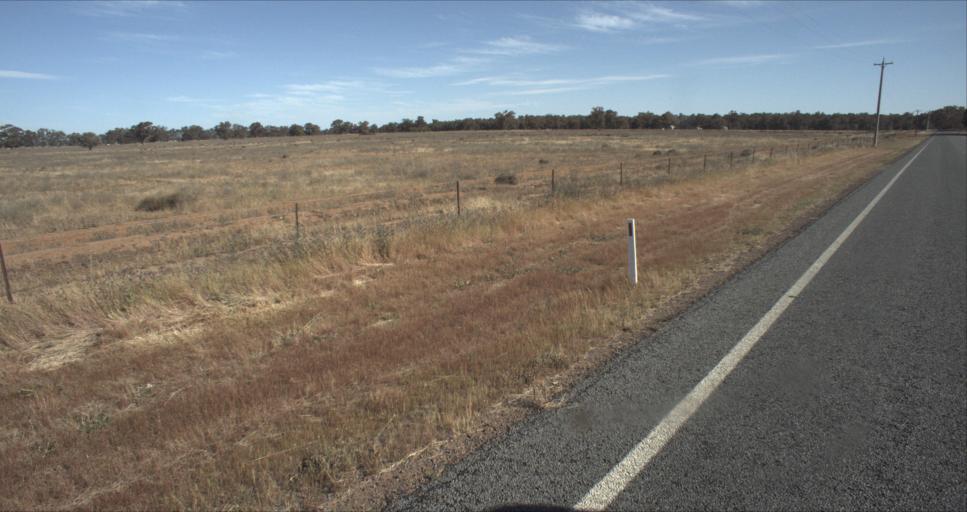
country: AU
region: New South Wales
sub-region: Leeton
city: Leeton
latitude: -34.6188
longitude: 146.3987
